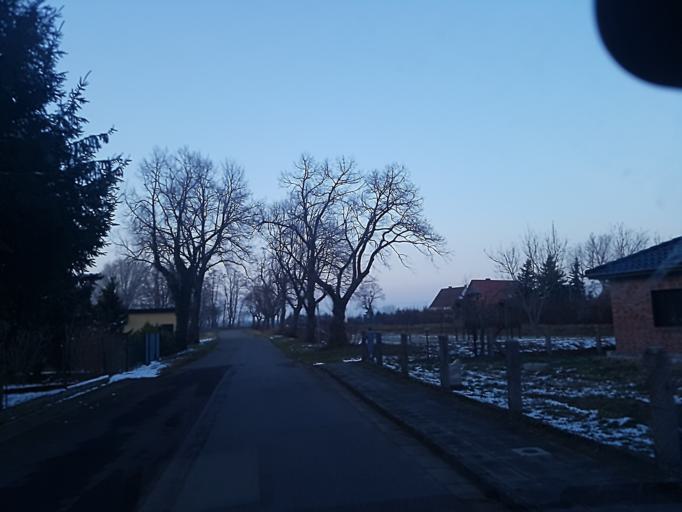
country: DE
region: Brandenburg
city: Bad Liebenwerda
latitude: 51.5149
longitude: 13.3451
